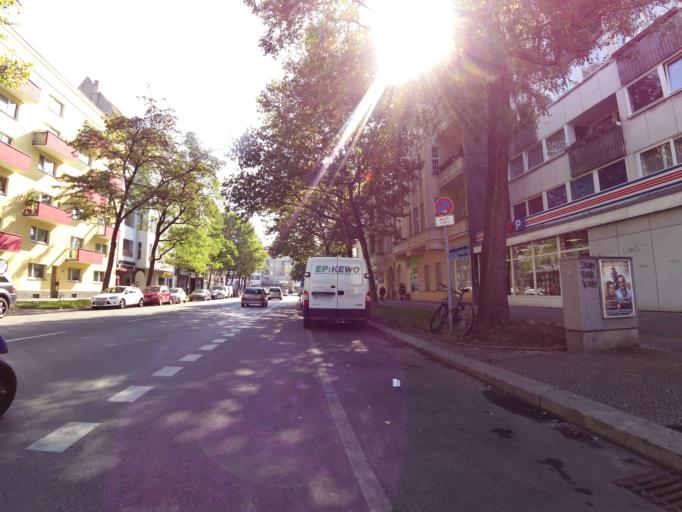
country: DE
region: Berlin
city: Berlin Schoeneberg
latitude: 52.4806
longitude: 13.3449
